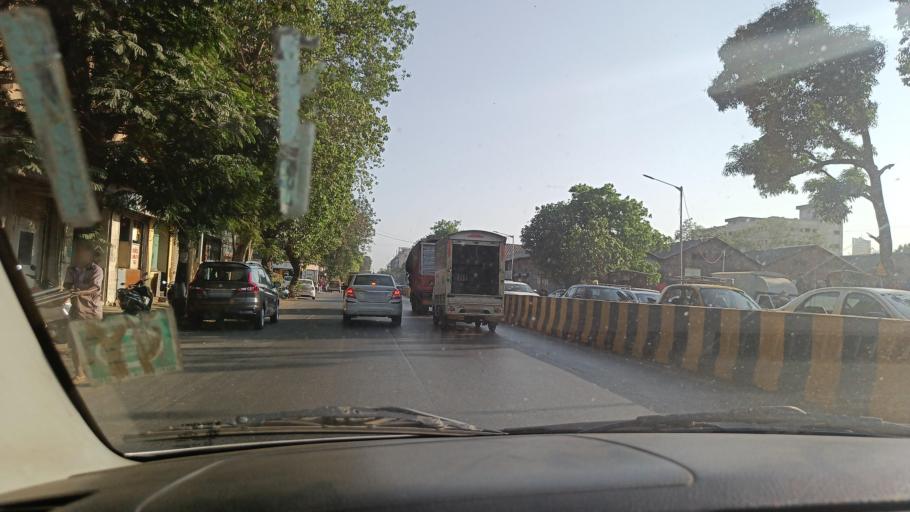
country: IN
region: Maharashtra
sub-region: Raigarh
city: Uran
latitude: 18.9551
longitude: 72.8421
